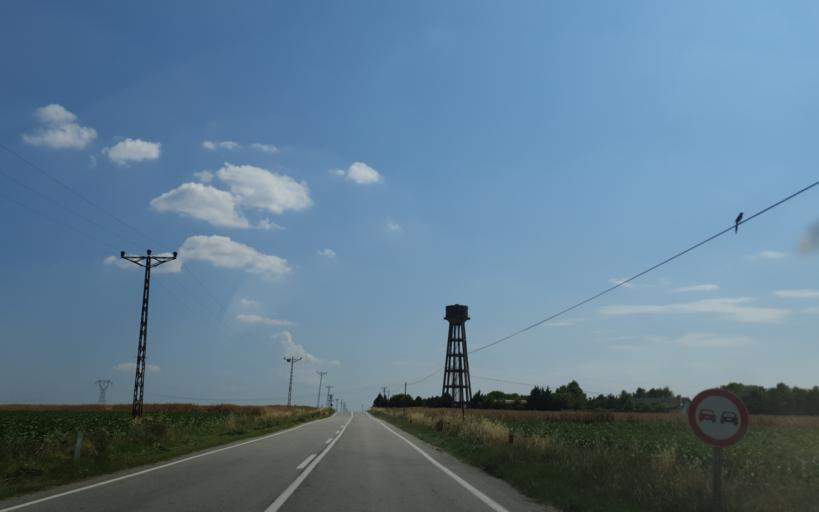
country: TR
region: Kirklareli
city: Buyukkaristiran
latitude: 41.3463
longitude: 27.5478
